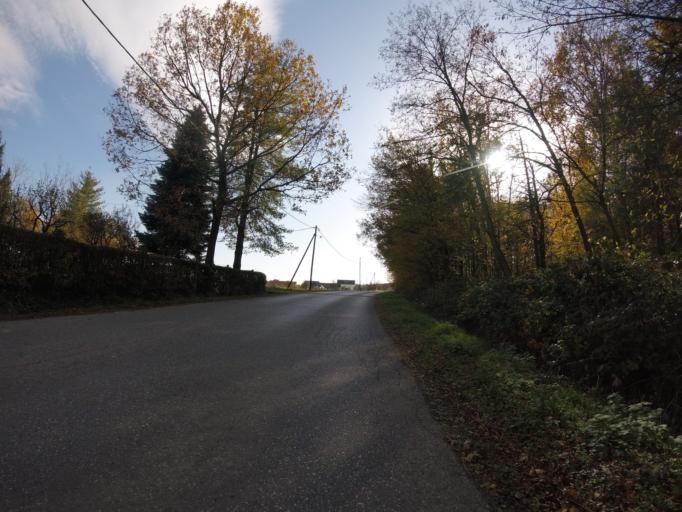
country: HR
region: Zagrebacka
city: Mraclin
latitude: 45.6217
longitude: 16.0714
